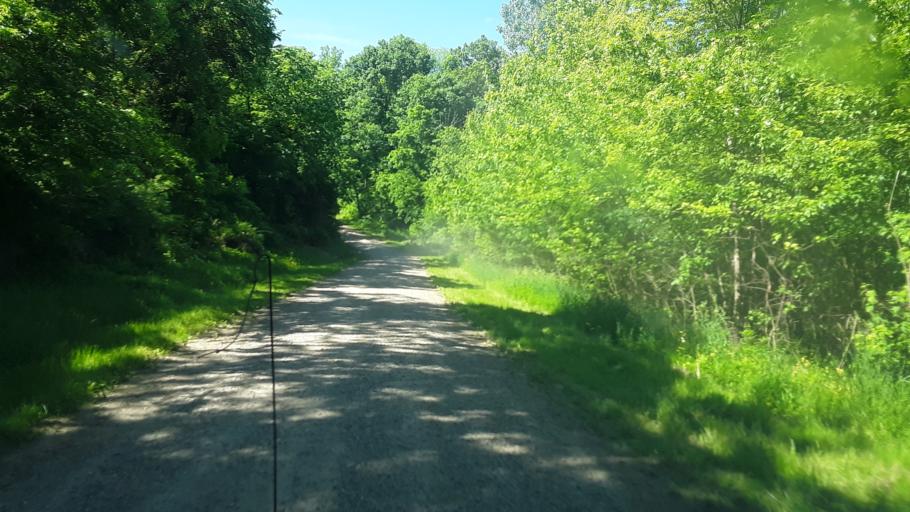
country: US
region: Ohio
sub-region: Coshocton County
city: West Lafayette
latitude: 40.1968
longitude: -81.6894
